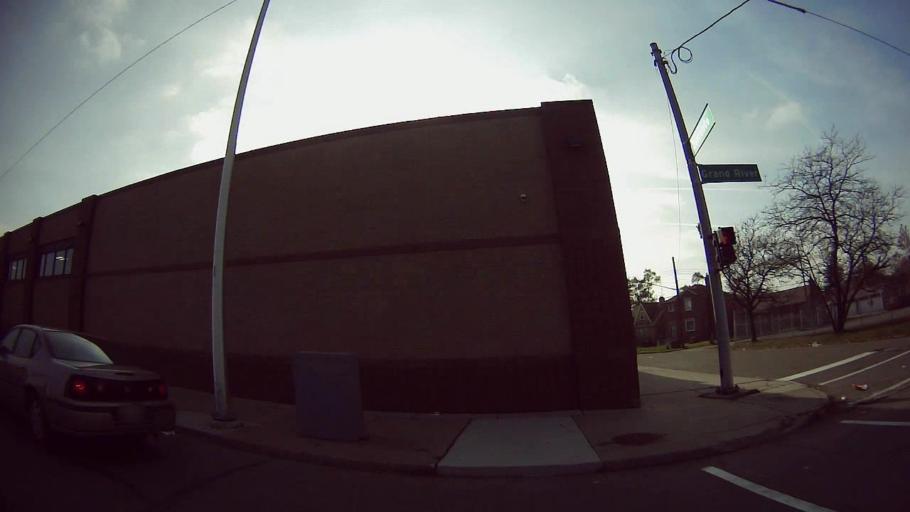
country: US
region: Michigan
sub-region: Wayne County
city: Dearborn
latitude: 42.3819
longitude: -83.1718
